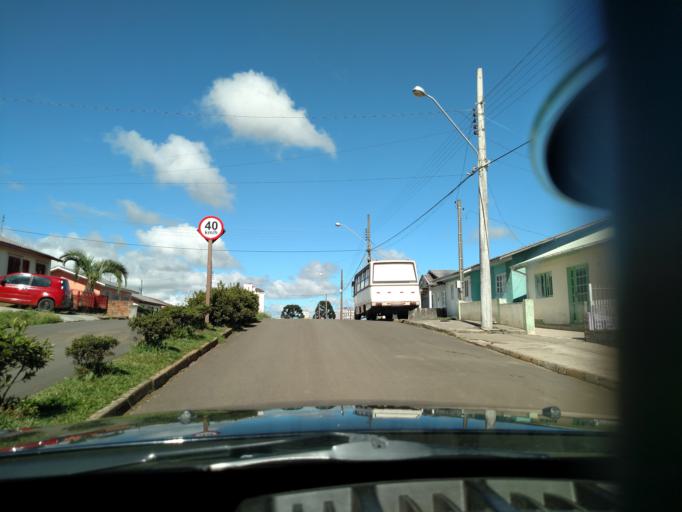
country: BR
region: Santa Catarina
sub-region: Sao Joaquim
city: Sao Joaquim
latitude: -28.2915
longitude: -49.9274
